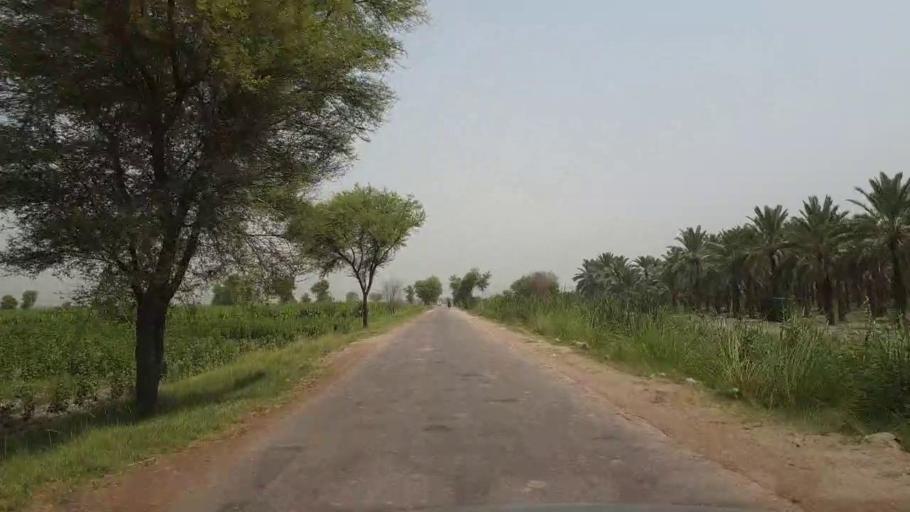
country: PK
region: Sindh
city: Gambat
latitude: 27.4059
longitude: 68.5506
